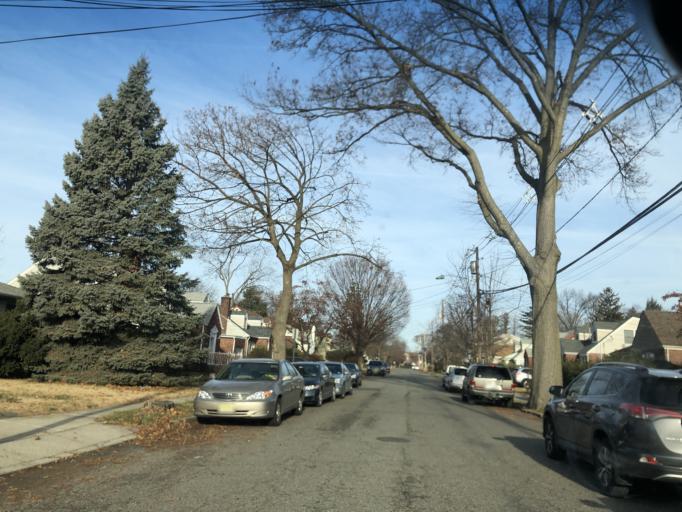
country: US
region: New Jersey
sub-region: Bergen County
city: Fair Lawn
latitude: 40.9331
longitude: -74.1267
